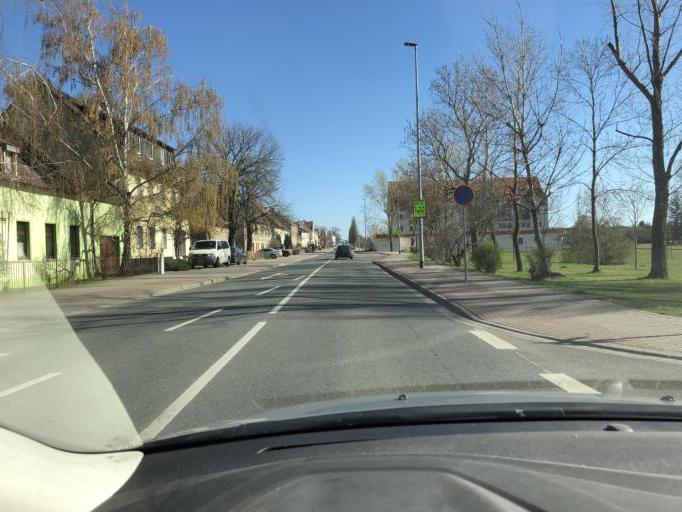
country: DE
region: Saxony-Anhalt
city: Stassfurt
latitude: 51.8608
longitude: 11.5932
